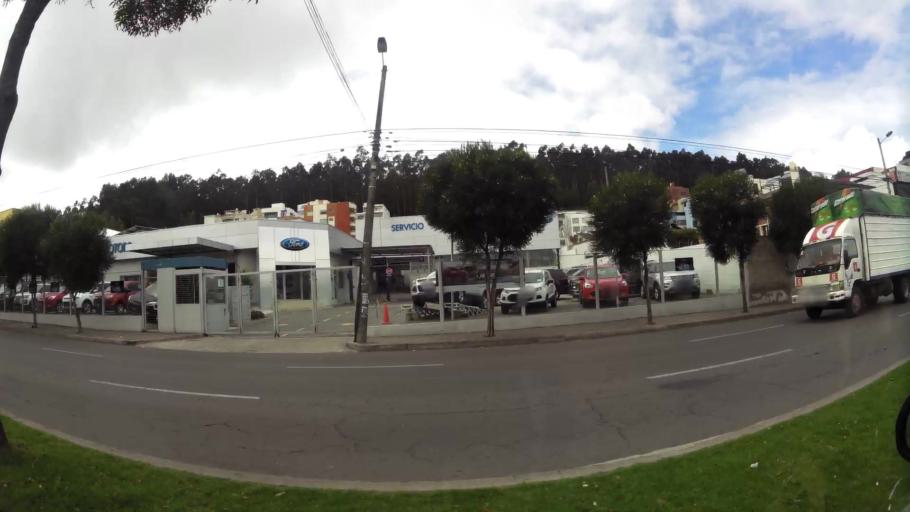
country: EC
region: Pichincha
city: Quito
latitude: -0.1648
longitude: -78.4659
